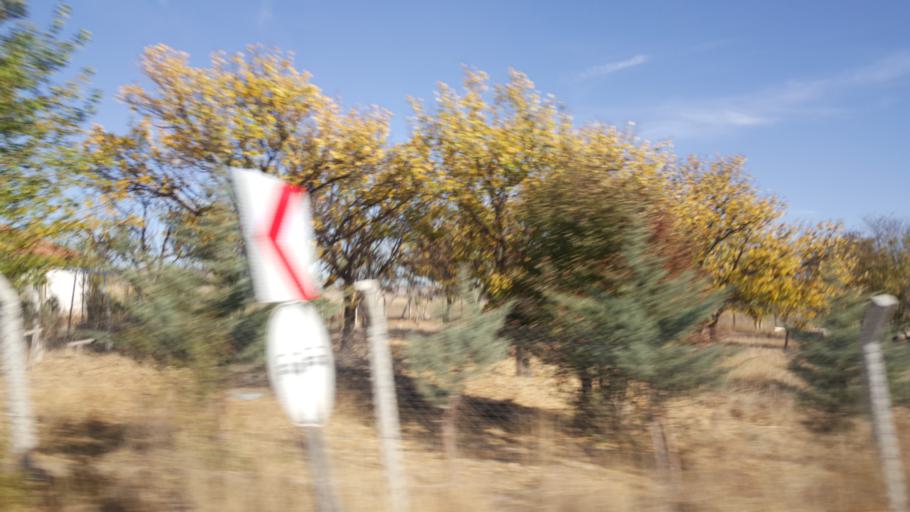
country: TR
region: Ankara
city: Yenice
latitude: 39.3134
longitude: 32.7571
